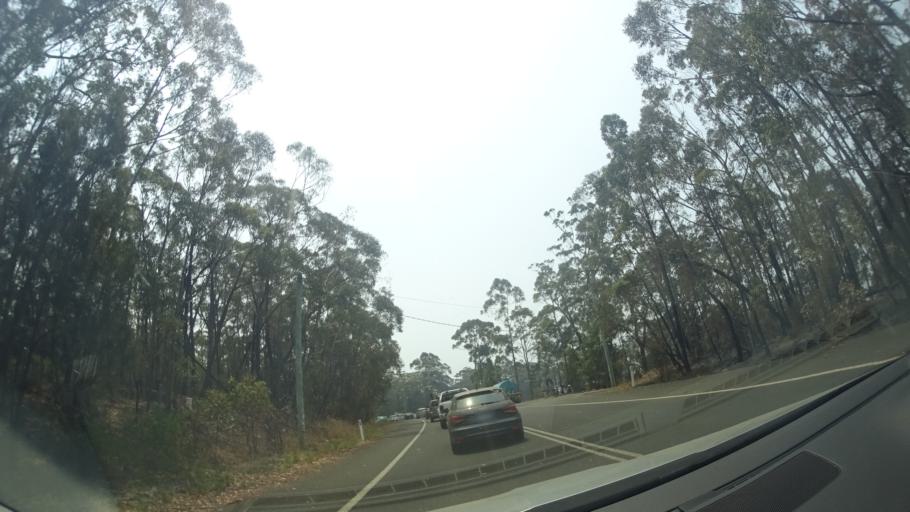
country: AU
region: New South Wales
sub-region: Shoalhaven Shire
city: Milton
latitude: -35.2215
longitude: 150.4685
